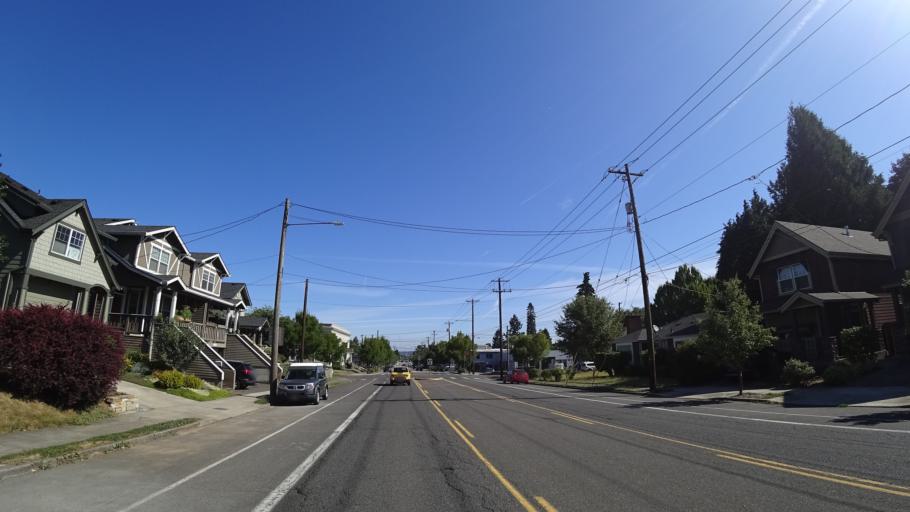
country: US
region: Oregon
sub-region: Multnomah County
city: Portland
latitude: 45.5805
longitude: -122.6870
